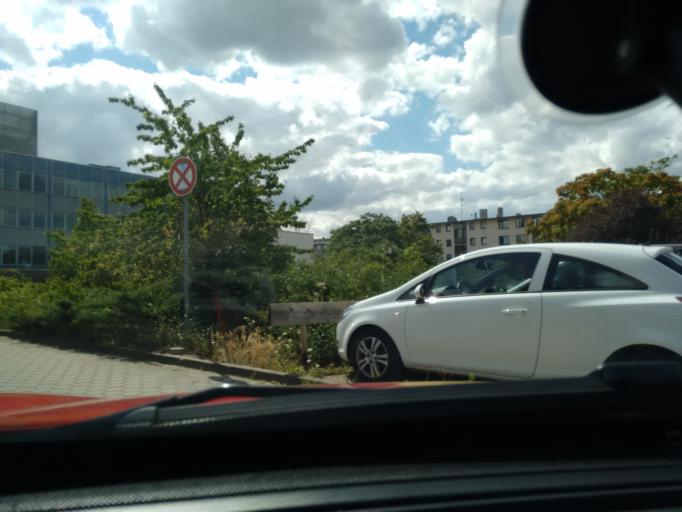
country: DE
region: Rheinland-Pfalz
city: Mainz
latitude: 49.9893
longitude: 8.2698
